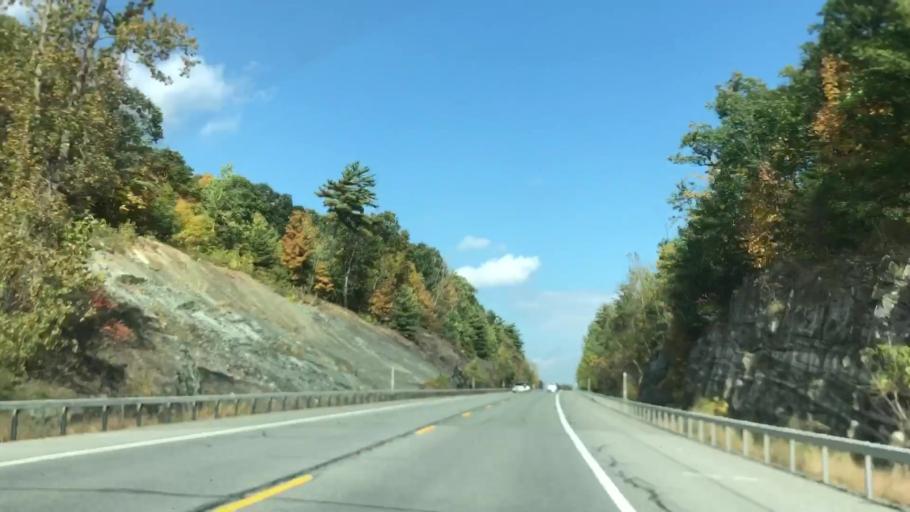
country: US
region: New York
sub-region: Washington County
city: Whitehall
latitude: 43.4522
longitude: -73.4485
